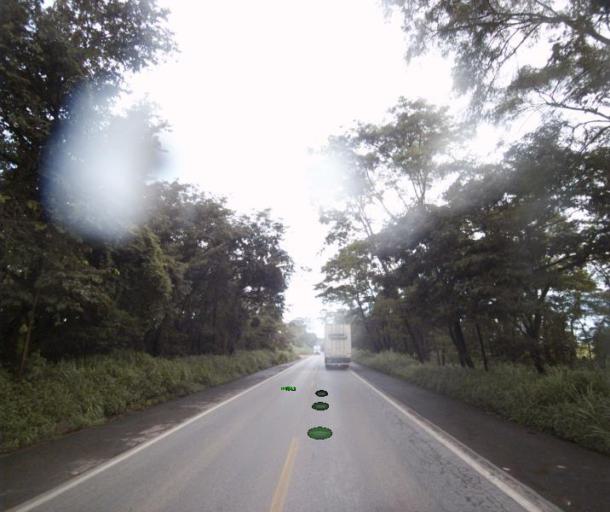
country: BR
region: Goias
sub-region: Porangatu
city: Porangatu
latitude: -13.9461
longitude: -49.0826
